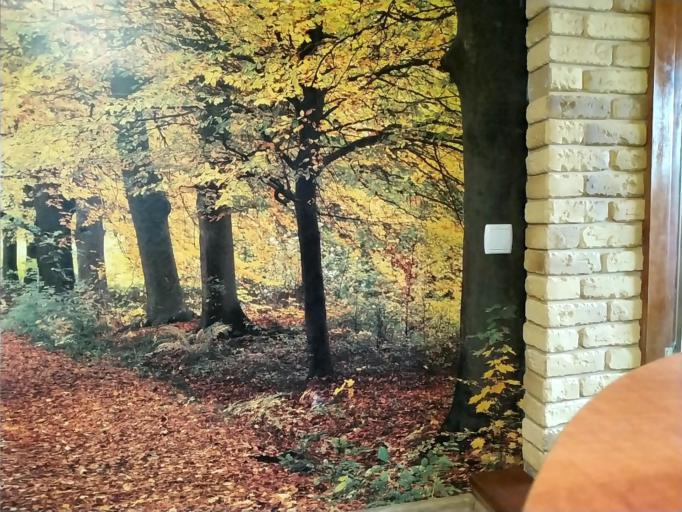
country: RU
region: Leningrad
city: Tolmachevo
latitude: 58.9432
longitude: 29.6631
